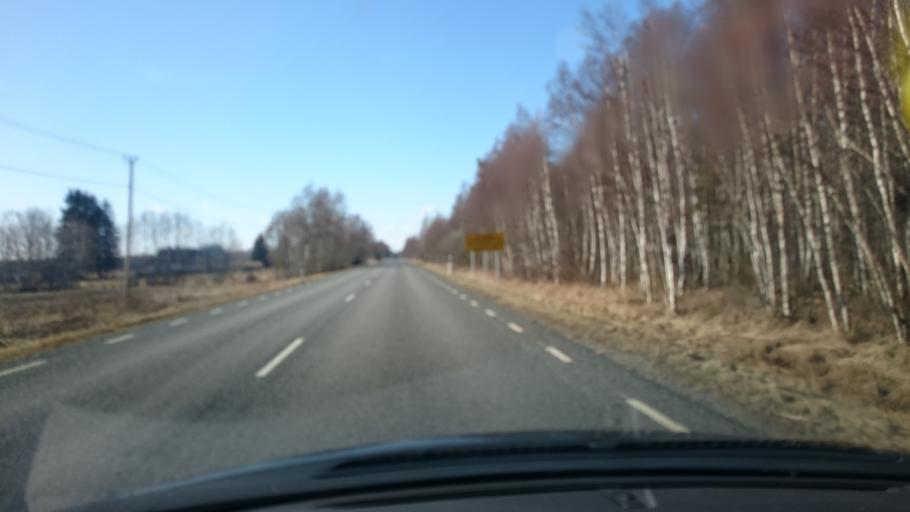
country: EE
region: Laeaene
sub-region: Lihula vald
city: Lihula
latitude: 58.6388
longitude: 23.8589
